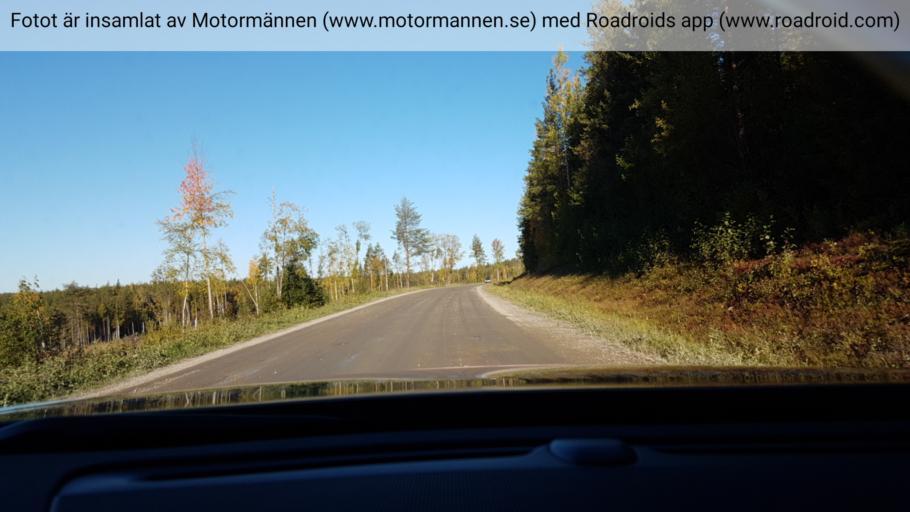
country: SE
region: Norrbotten
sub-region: Alvsbyns Kommun
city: AElvsbyn
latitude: 66.1905
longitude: 21.1975
